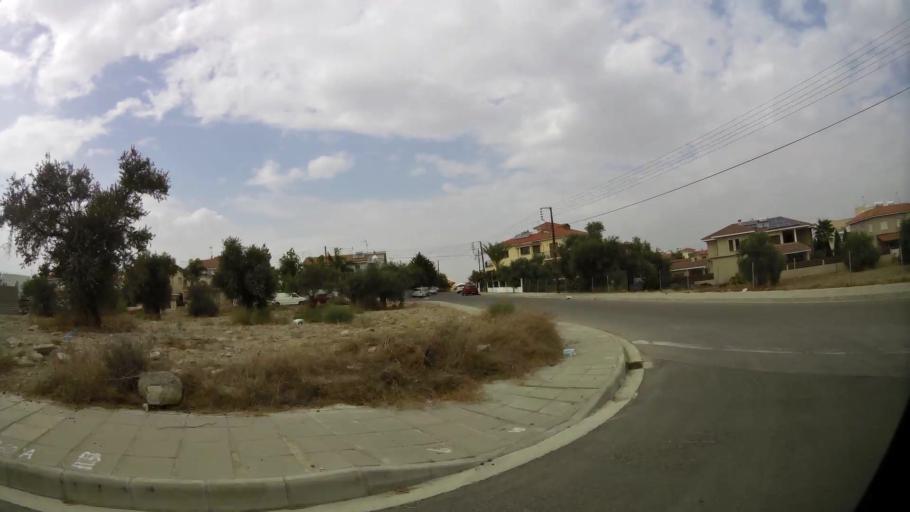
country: CY
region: Lefkosia
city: Geri
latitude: 35.0992
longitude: 33.3752
